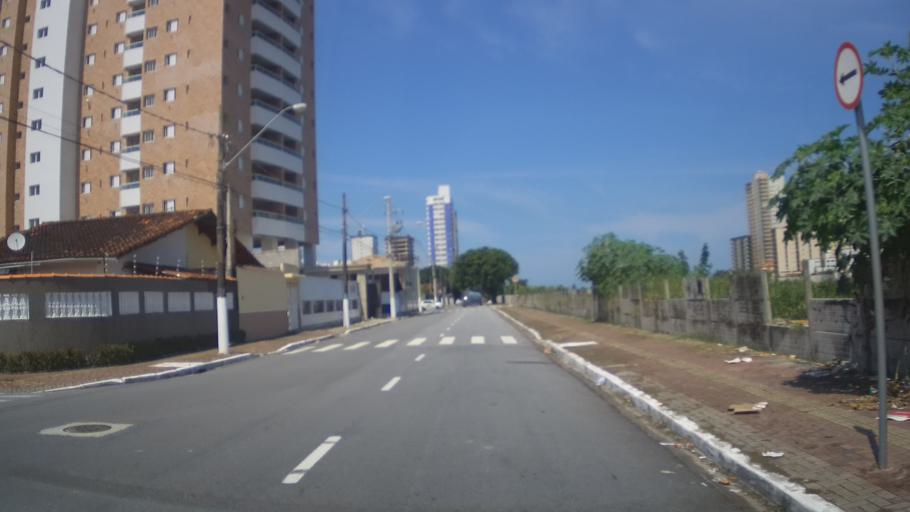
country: BR
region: Sao Paulo
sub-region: Praia Grande
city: Praia Grande
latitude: -24.0114
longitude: -46.4367
